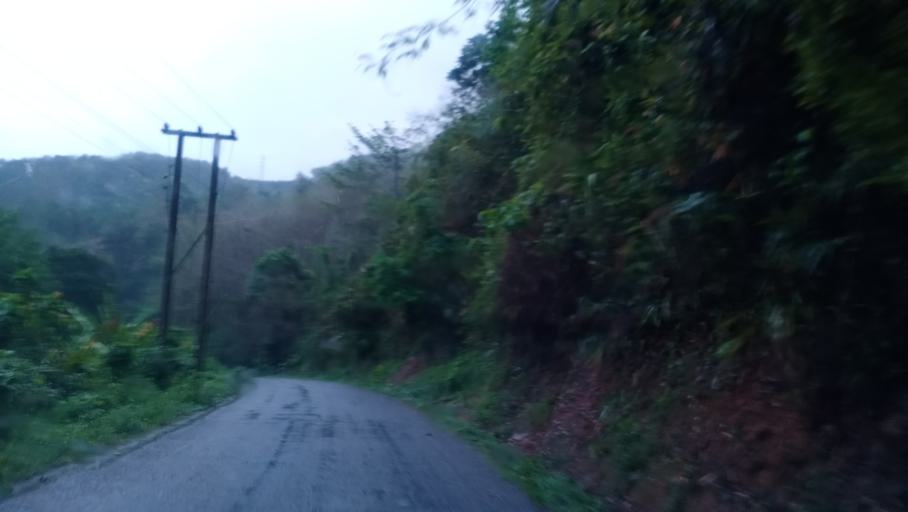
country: LA
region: Phongsali
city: Khoa
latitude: 21.0649
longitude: 102.4778
